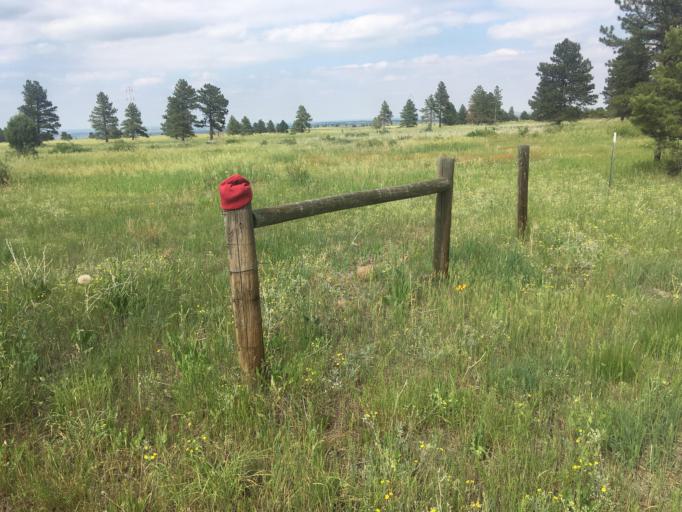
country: US
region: Colorado
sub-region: Boulder County
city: Superior
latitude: 39.9208
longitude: -105.2542
